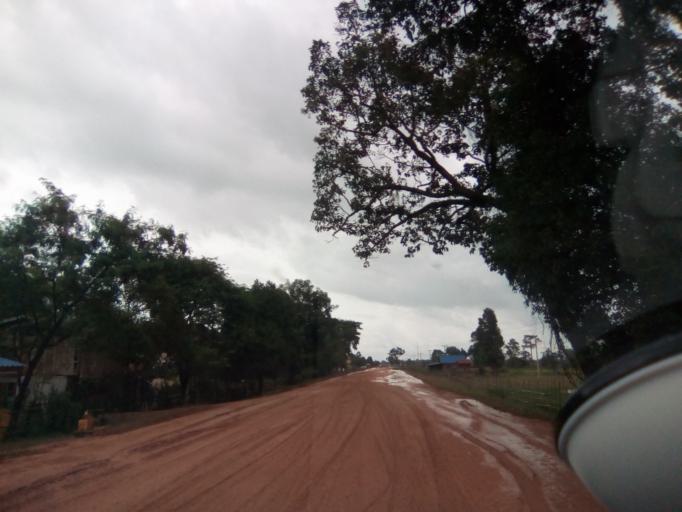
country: LA
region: Attapu
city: Attapu
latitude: 14.7615
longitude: 106.7124
